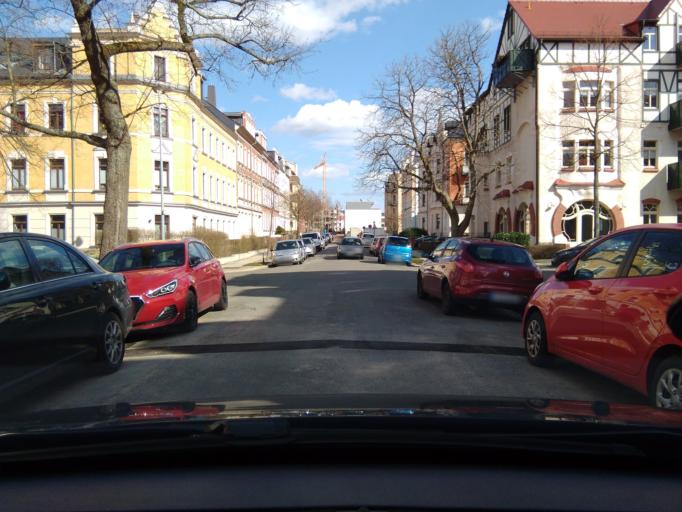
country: DE
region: Saxony
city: Chemnitz
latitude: 50.8330
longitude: 12.8890
